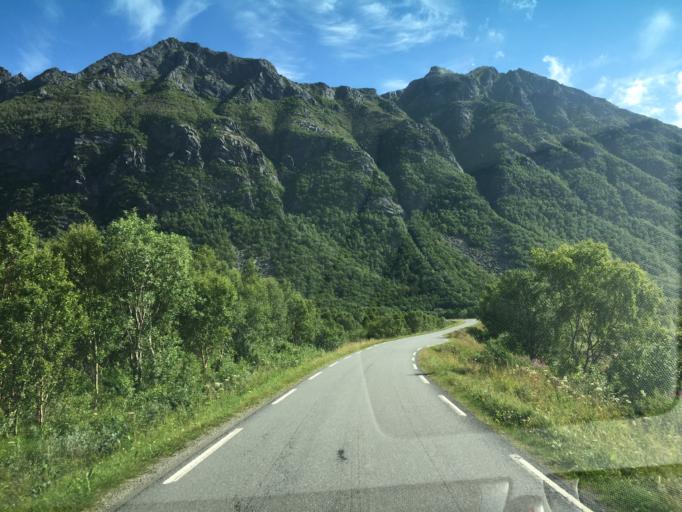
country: NO
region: Nordland
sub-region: Vagan
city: Svolvaer
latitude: 68.3991
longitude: 14.5736
